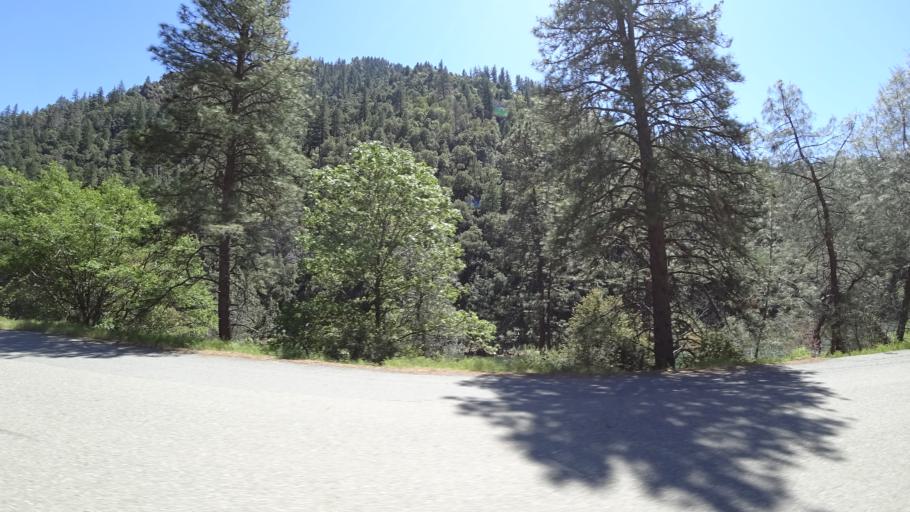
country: US
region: California
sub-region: Humboldt County
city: Willow Creek
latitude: 40.7986
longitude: -123.3969
